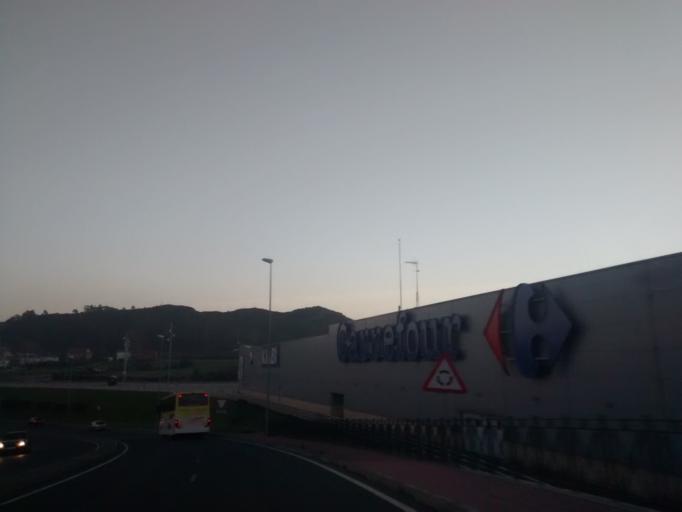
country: ES
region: Cantabria
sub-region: Provincia de Cantabria
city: Santa Cruz de Bezana
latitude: 43.4587
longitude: -3.8613
